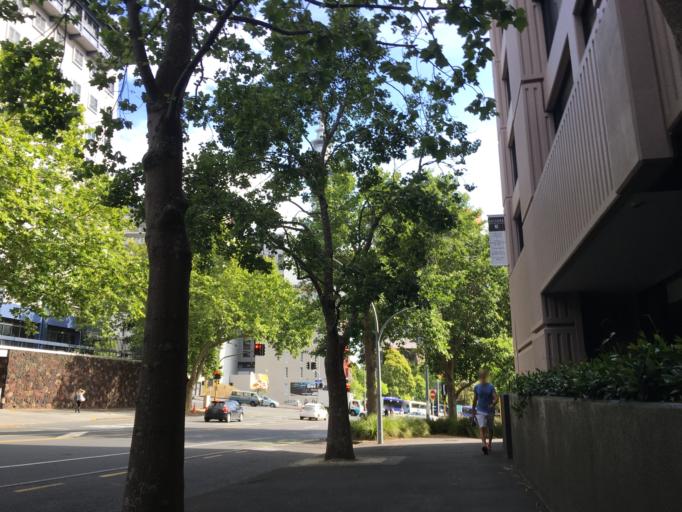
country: NZ
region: Auckland
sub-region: Auckland
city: Auckland
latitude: -36.8526
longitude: 174.7604
